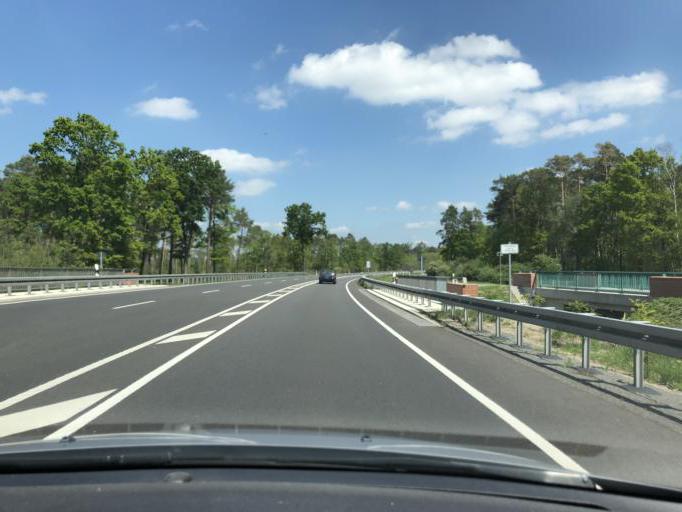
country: DE
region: Saxony
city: Zinna
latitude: 51.5294
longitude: 12.8876
